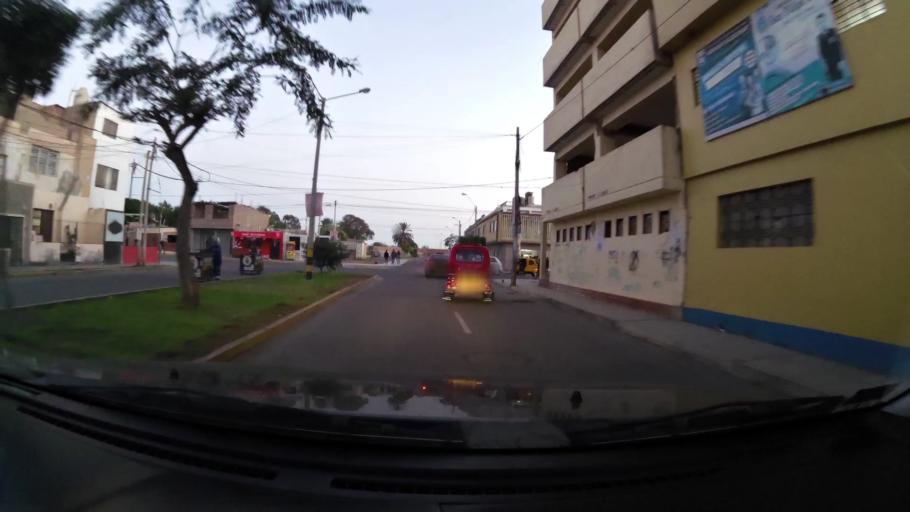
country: PE
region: Ica
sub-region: Provincia de Pisco
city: Pisco
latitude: -13.7094
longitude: -76.2087
